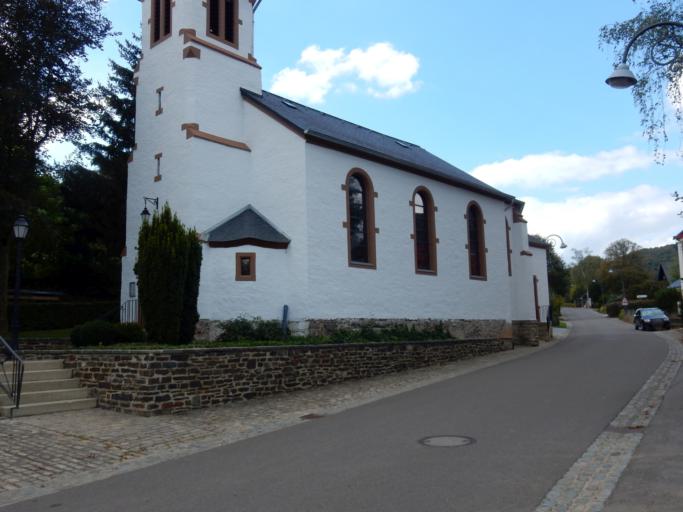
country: LU
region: Diekirch
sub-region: Canton de Wiltz
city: Goesdorf
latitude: 49.9107
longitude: 5.9946
